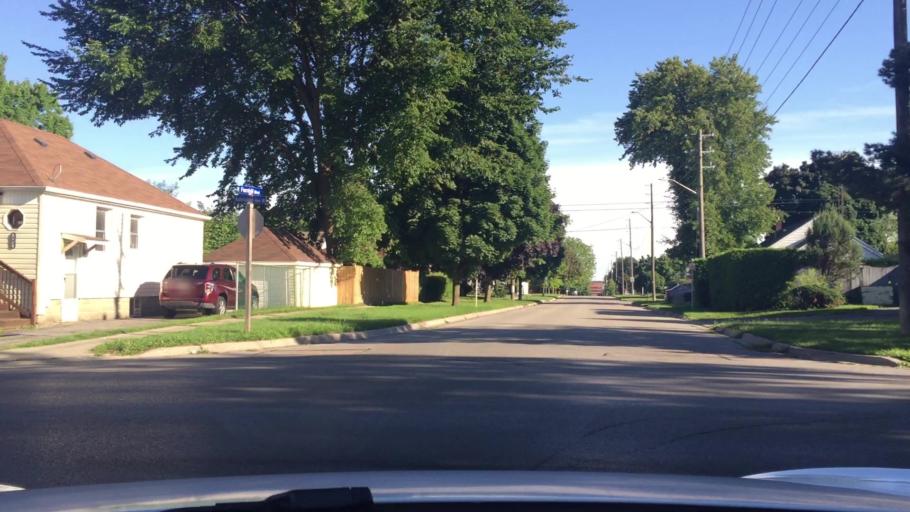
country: CA
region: Ontario
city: Oshawa
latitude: 43.8995
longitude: -78.8834
